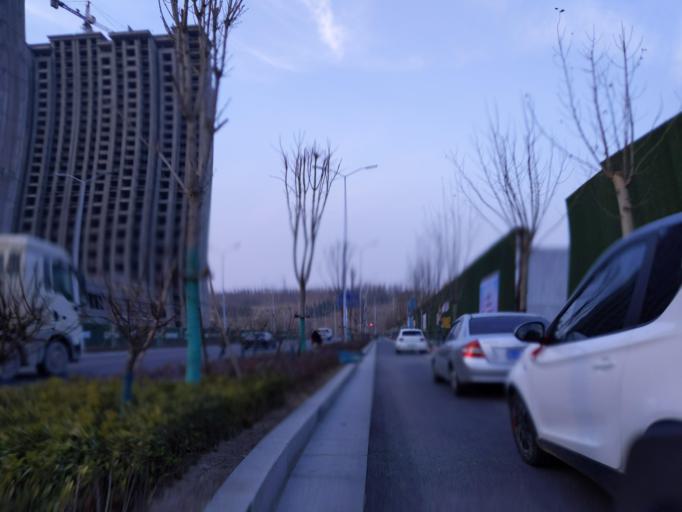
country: CN
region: Henan Sheng
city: Puyang
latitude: 35.8154
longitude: 115.0118
